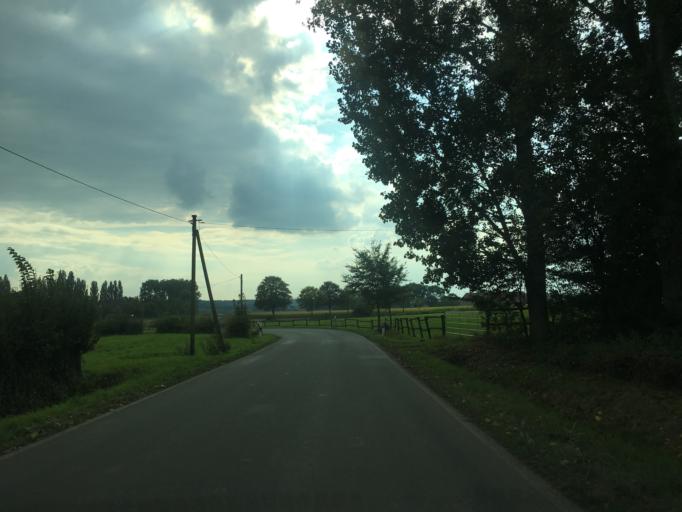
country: DE
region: North Rhine-Westphalia
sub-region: Regierungsbezirk Munster
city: Ascheberg
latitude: 51.7630
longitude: 7.5828
